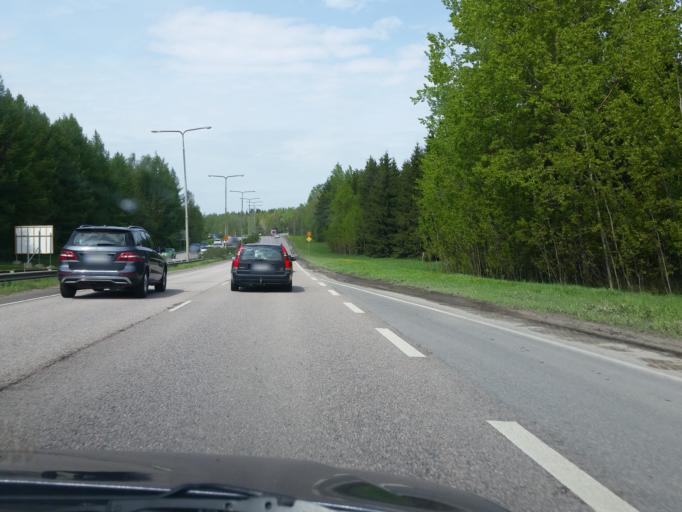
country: FI
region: Uusimaa
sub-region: Helsinki
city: Helsinki
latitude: 60.2245
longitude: 24.9084
